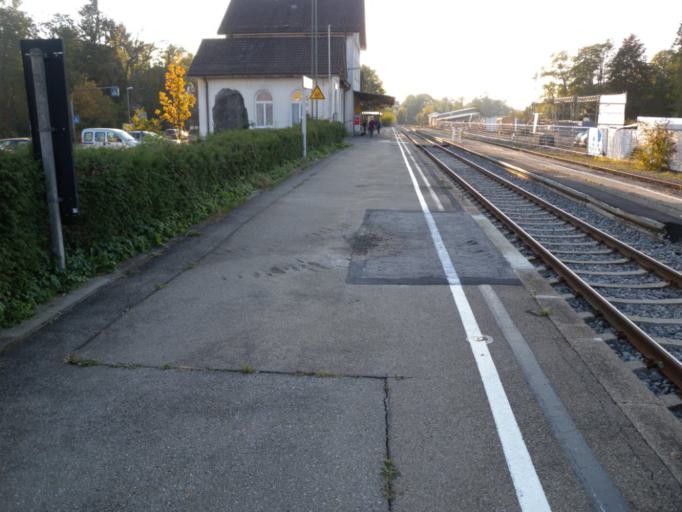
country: DE
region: Baden-Wuerttemberg
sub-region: Tuebingen Region
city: Bad Waldsee
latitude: 47.9252
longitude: 9.7531
